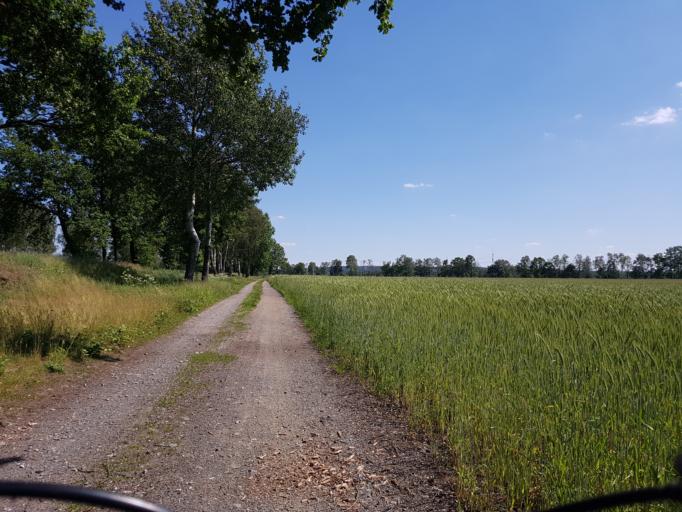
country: DE
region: Brandenburg
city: Elsterwerda
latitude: 51.4360
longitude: 13.5358
